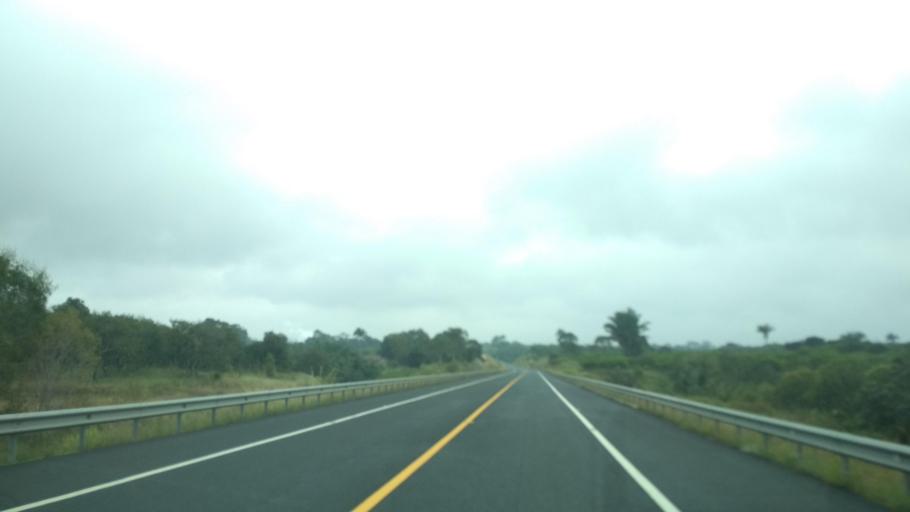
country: MX
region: Veracruz
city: Vega de San Marcos
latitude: 20.1835
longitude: -96.9663
